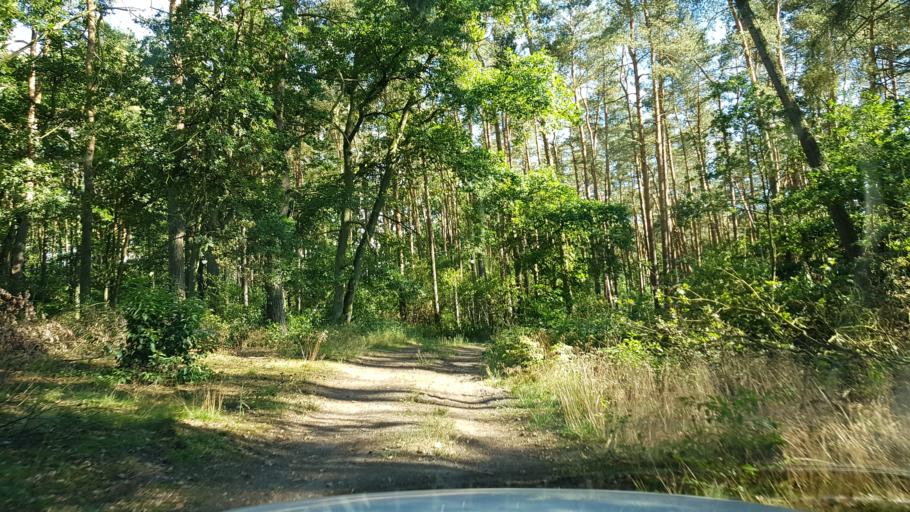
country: PL
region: West Pomeranian Voivodeship
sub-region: Powiat goleniowski
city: Goleniow
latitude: 53.5605
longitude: 14.7526
